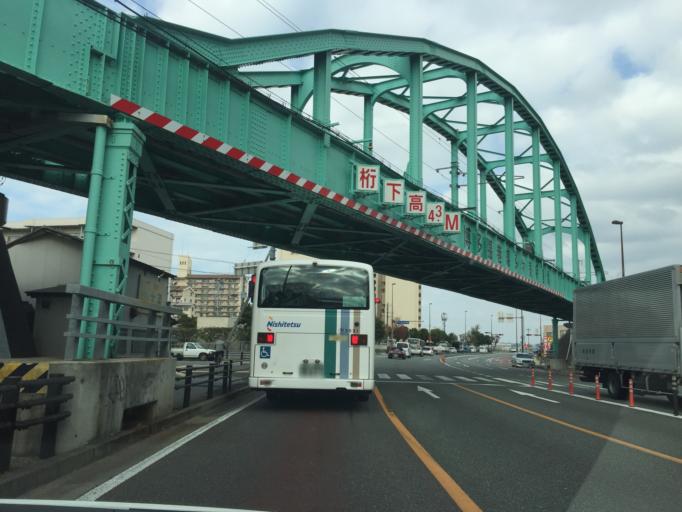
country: JP
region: Fukuoka
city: Fukuoka-shi
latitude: 33.6369
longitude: 130.4248
